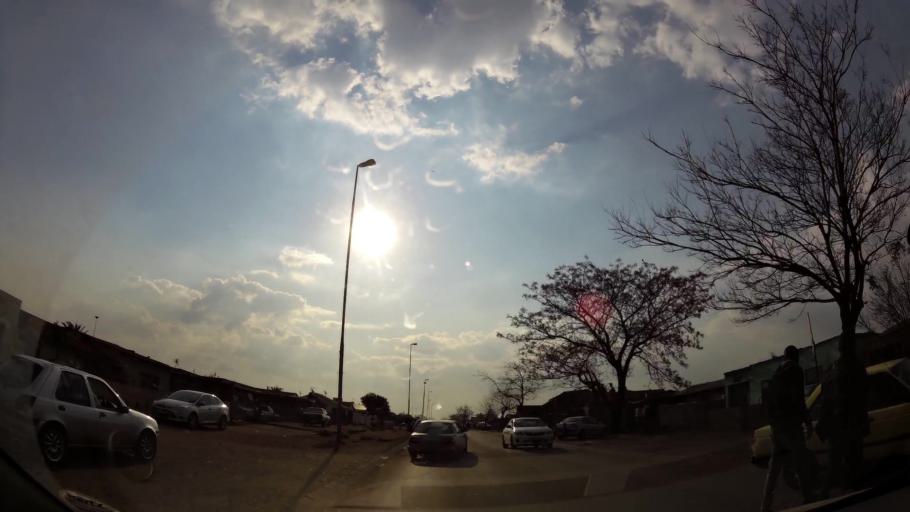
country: ZA
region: Gauteng
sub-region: Ekurhuleni Metropolitan Municipality
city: Germiston
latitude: -26.3563
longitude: 28.2060
